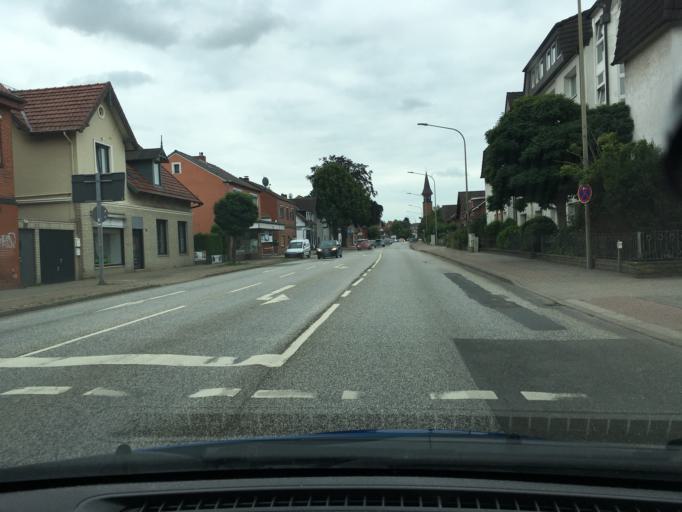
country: DE
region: Schleswig-Holstein
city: Geesthacht
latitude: 53.4429
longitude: 10.3636
